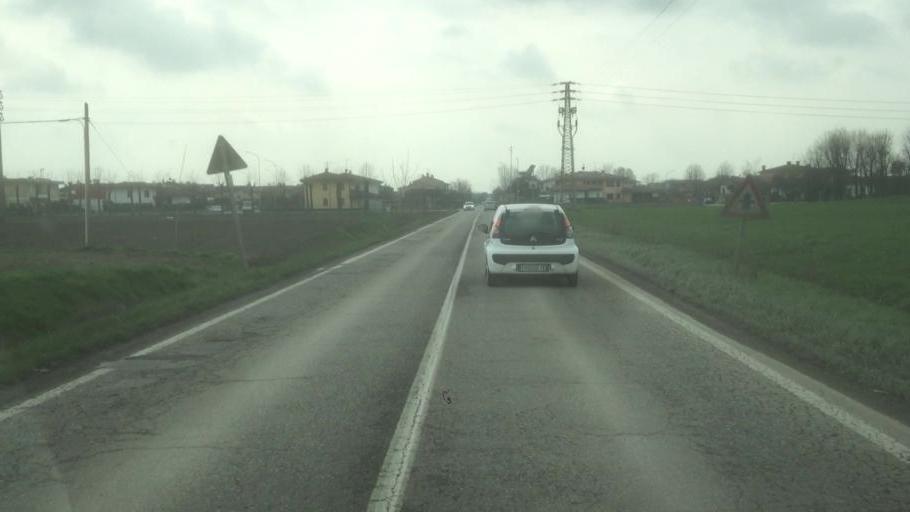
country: IT
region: Lombardy
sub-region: Provincia di Mantova
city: Casaloldo
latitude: 45.2604
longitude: 10.4769
